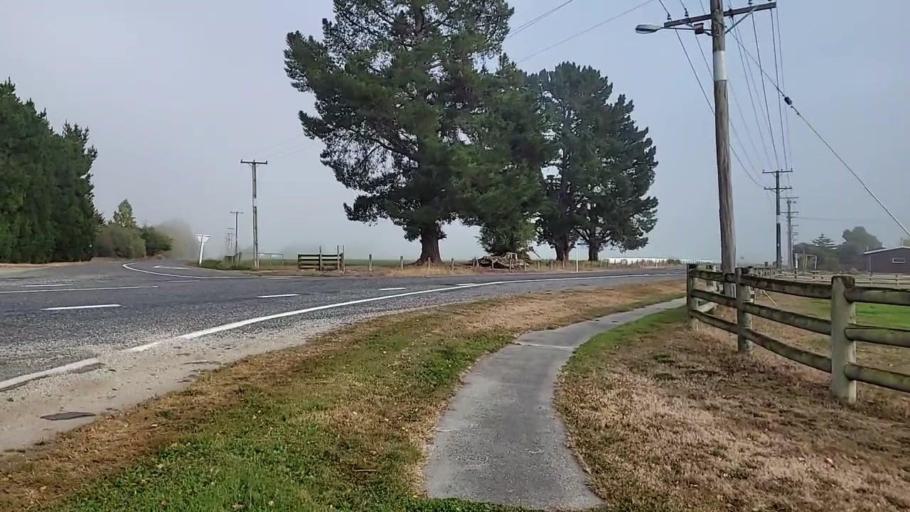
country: NZ
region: Southland
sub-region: Gore District
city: Gore
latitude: -45.6331
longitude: 169.3623
